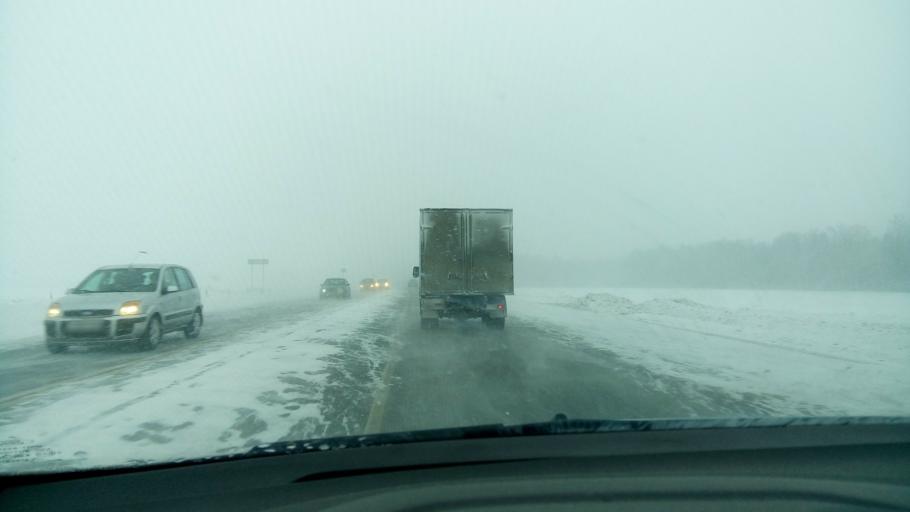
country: RU
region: Sverdlovsk
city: Bogdanovich
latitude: 56.7739
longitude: 61.9450
